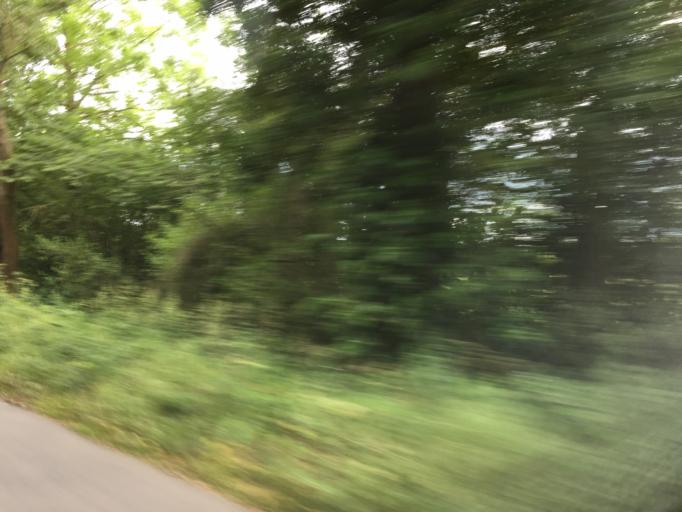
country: GB
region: England
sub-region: Wiltshire
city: Leigh
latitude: 51.6400
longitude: -1.9236
